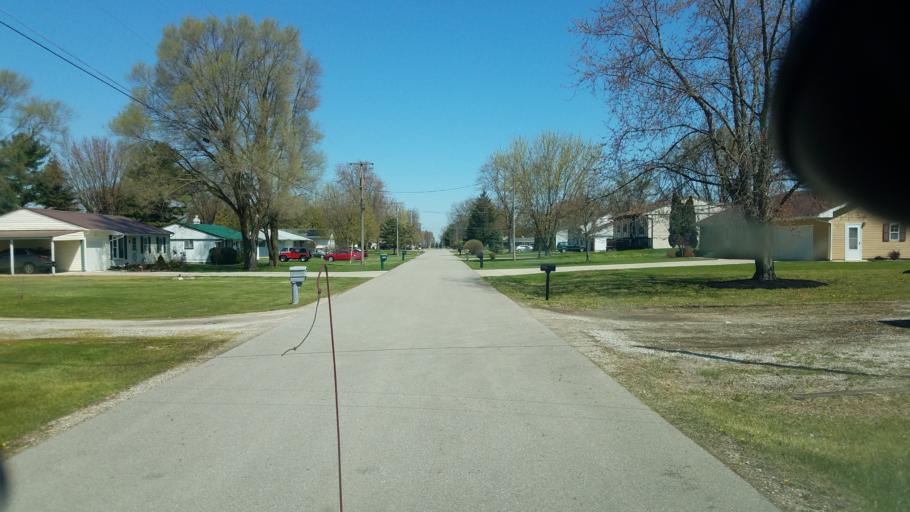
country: US
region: Ohio
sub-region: Marion County
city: Marion
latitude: 40.6375
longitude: -83.0772
